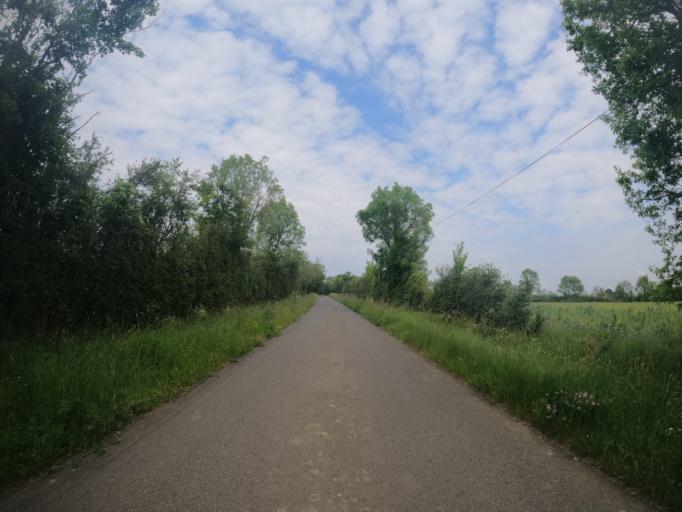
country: FR
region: Poitou-Charentes
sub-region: Departement des Deux-Sevres
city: Saint-Varent
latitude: 46.8769
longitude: -0.2820
